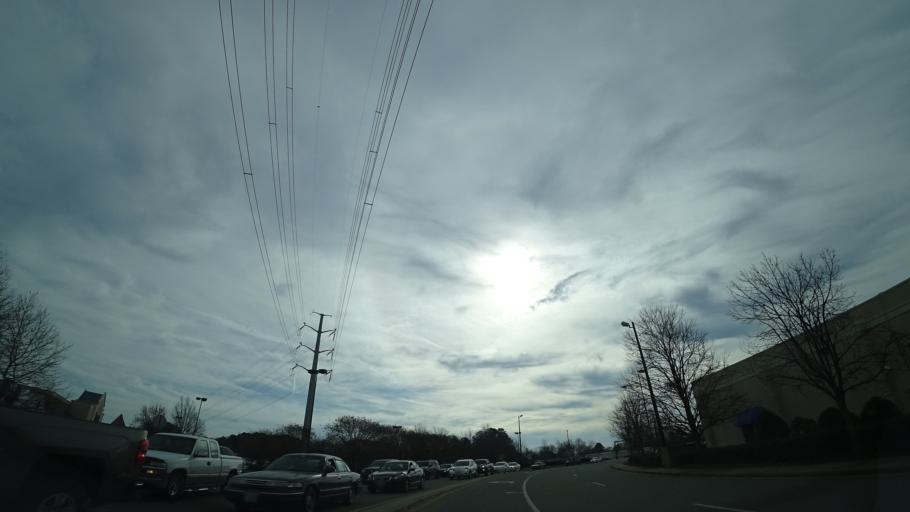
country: US
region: Virginia
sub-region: City of Hampton
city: Hampton
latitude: 37.0389
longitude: -76.3986
